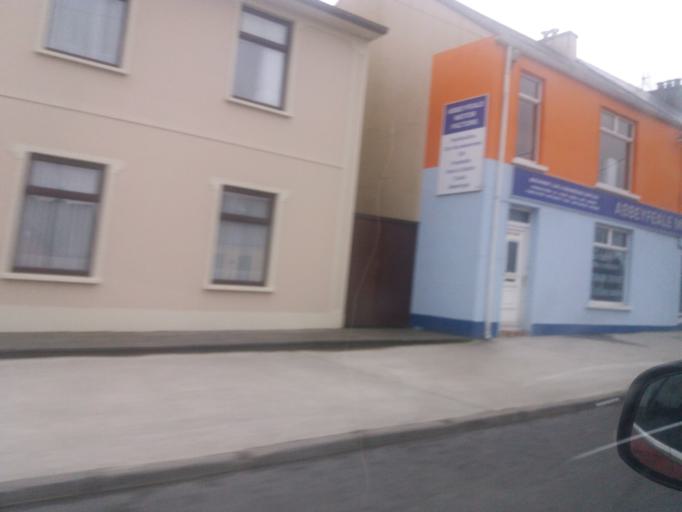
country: IE
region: Munster
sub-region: County Limerick
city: Abbeyfeale
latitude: 52.3823
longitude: -9.3015
